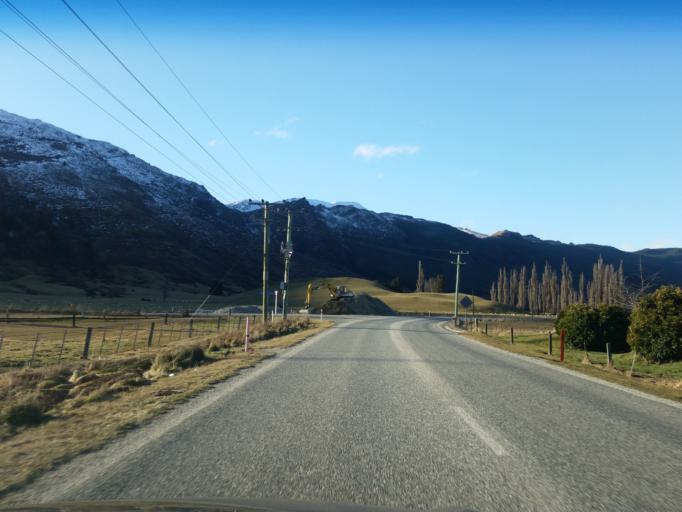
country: NZ
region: Otago
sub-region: Queenstown-Lakes District
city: Arrowtown
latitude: -44.9539
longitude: 168.7444
